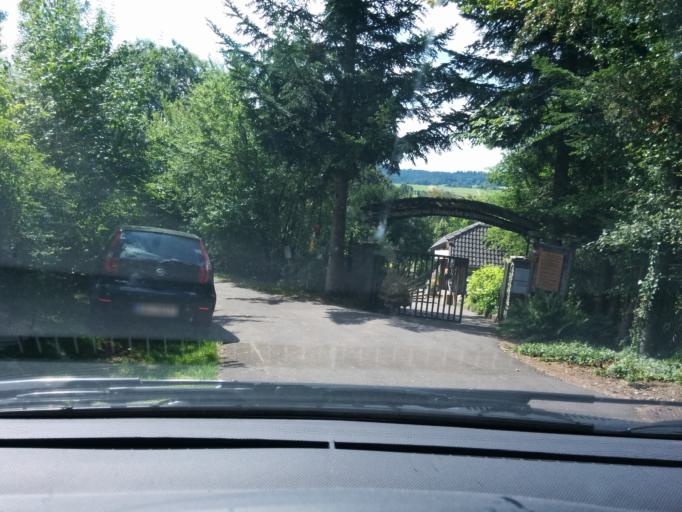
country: AT
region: Upper Austria
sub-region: Politischer Bezirk Rohrbach
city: Ulrichsberg
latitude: 48.6936
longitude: 13.8841
